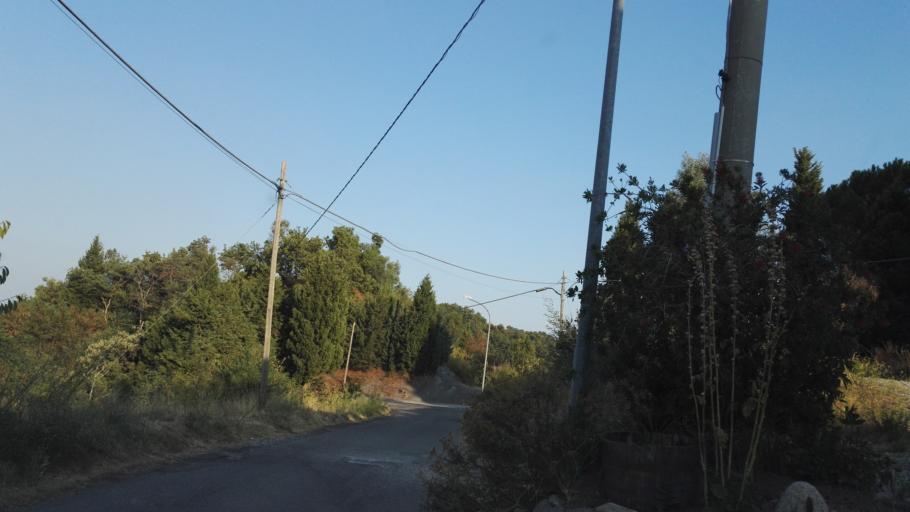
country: IT
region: Calabria
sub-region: Provincia di Reggio Calabria
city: Caulonia
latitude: 38.4055
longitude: 16.3640
